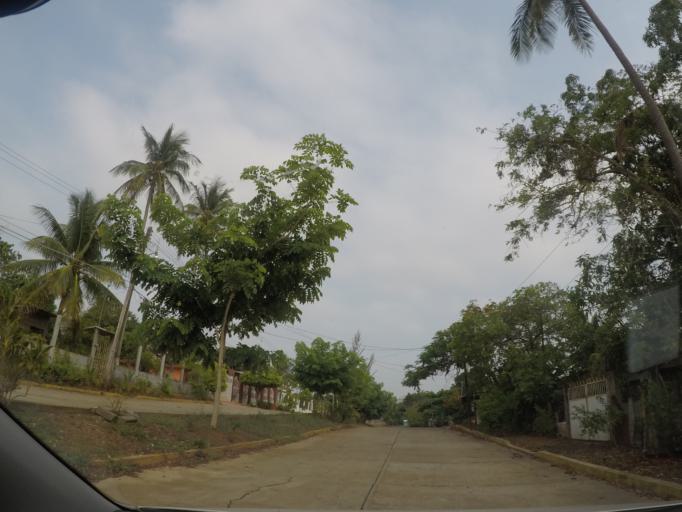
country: MX
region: Oaxaca
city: Colonia Rincon Viejo
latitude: 16.8813
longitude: -95.0452
